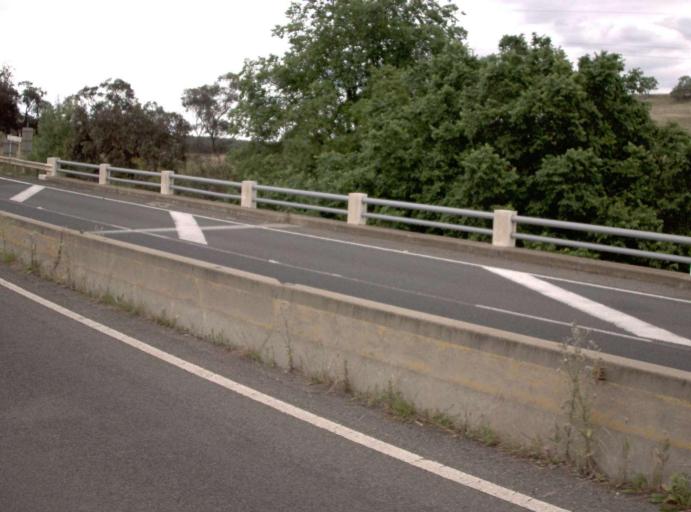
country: AU
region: Victoria
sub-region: Melton
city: Brookfield
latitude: -37.6857
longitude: 144.5149
